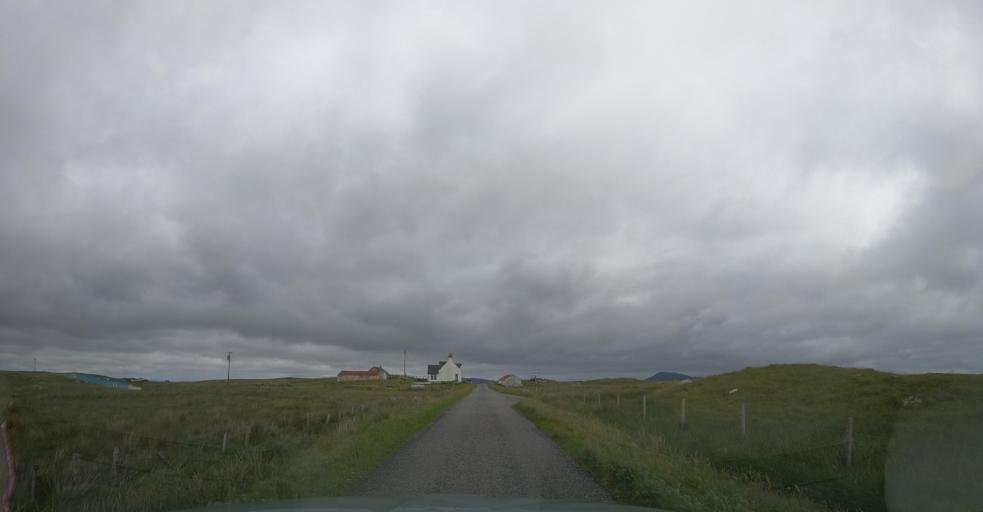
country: GB
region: Scotland
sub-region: Eilean Siar
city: Isle of North Uist
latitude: 57.5417
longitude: -7.3410
